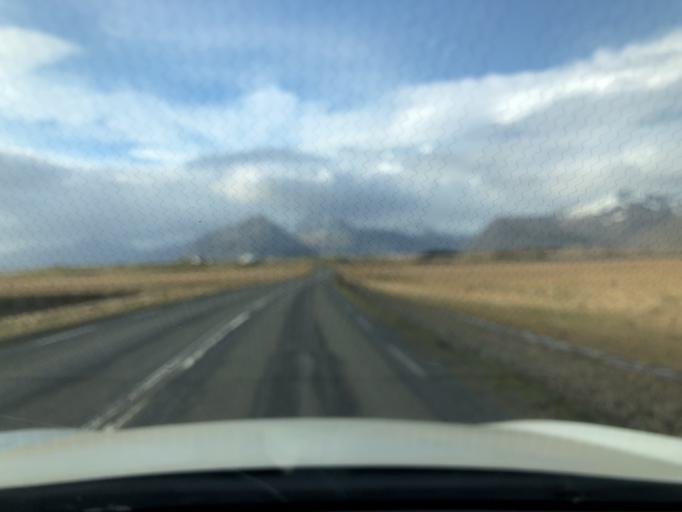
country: IS
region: East
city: Hoefn
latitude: 64.2700
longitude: -15.2024
